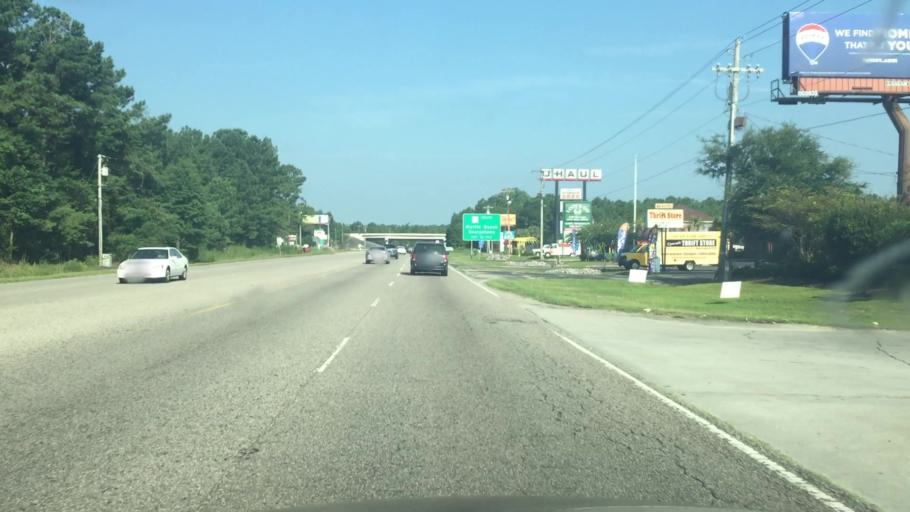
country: US
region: South Carolina
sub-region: Horry County
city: North Myrtle Beach
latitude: 33.8733
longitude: -78.6761
